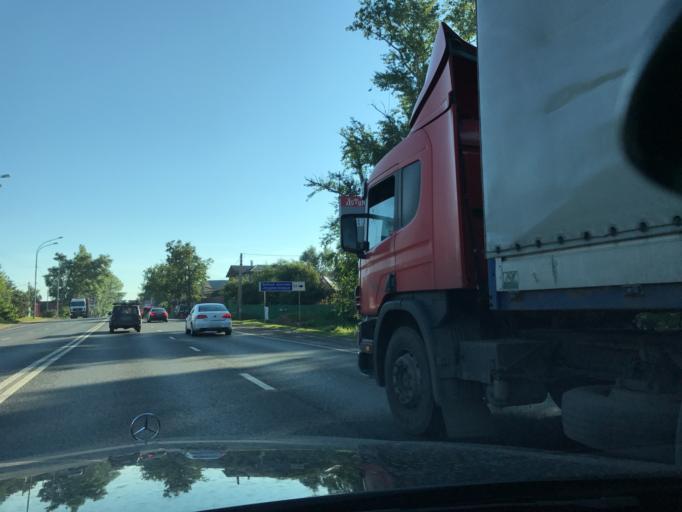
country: RU
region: Moskovskaya
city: Medvezh'i Ozera
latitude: 55.8532
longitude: 37.9732
